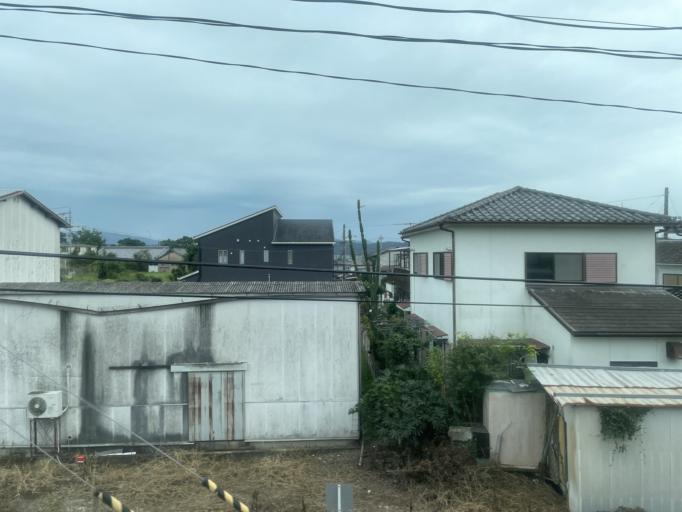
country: JP
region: Wakayama
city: Wakayama-shi
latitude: 34.2679
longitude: 135.2265
